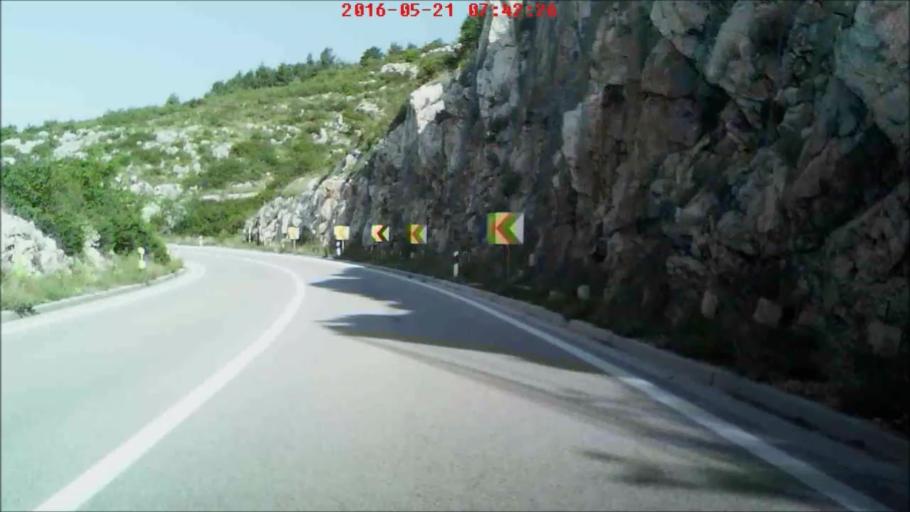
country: HR
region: Dubrovacko-Neretvanska
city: Podgora
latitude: 42.8106
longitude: 17.8036
